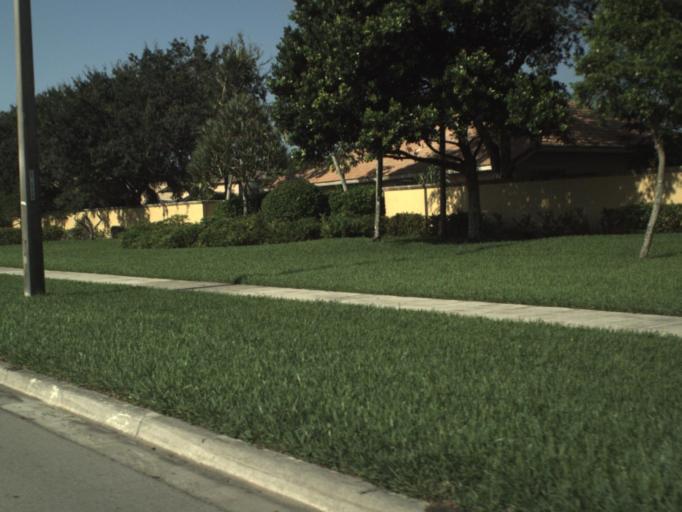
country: US
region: Florida
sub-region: Broward County
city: Parkland
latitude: 26.2923
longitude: -80.2021
